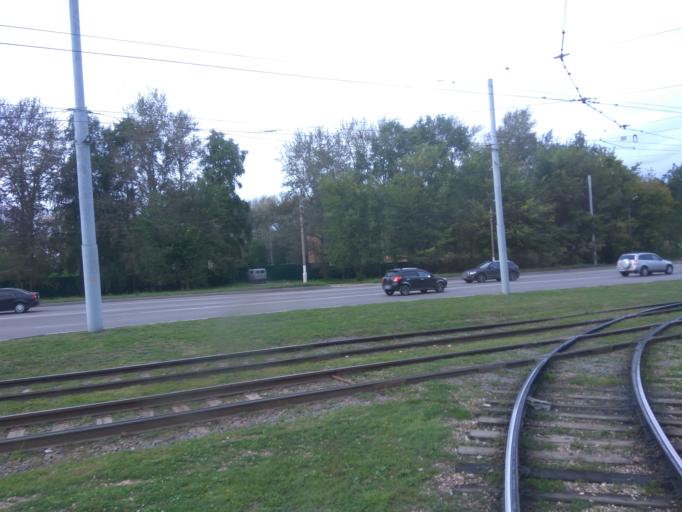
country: RU
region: Moskovskaya
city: Kolomna
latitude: 55.0674
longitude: 38.7536
